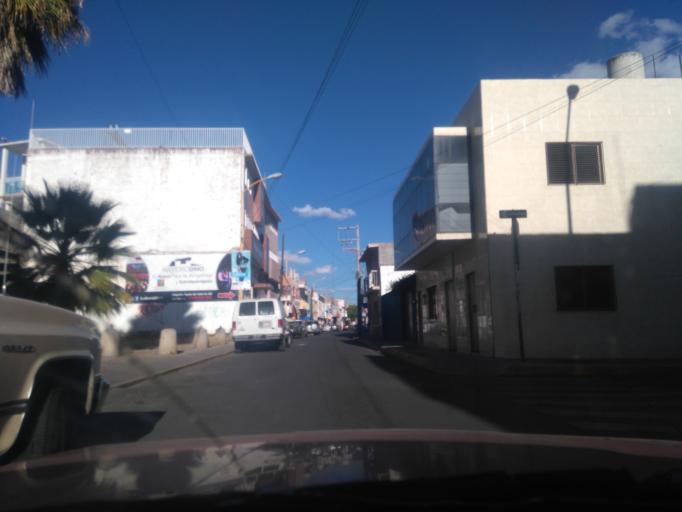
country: MX
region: Aguascalientes
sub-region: Aguascalientes
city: Aguascalientes
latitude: 21.8780
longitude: -102.3031
